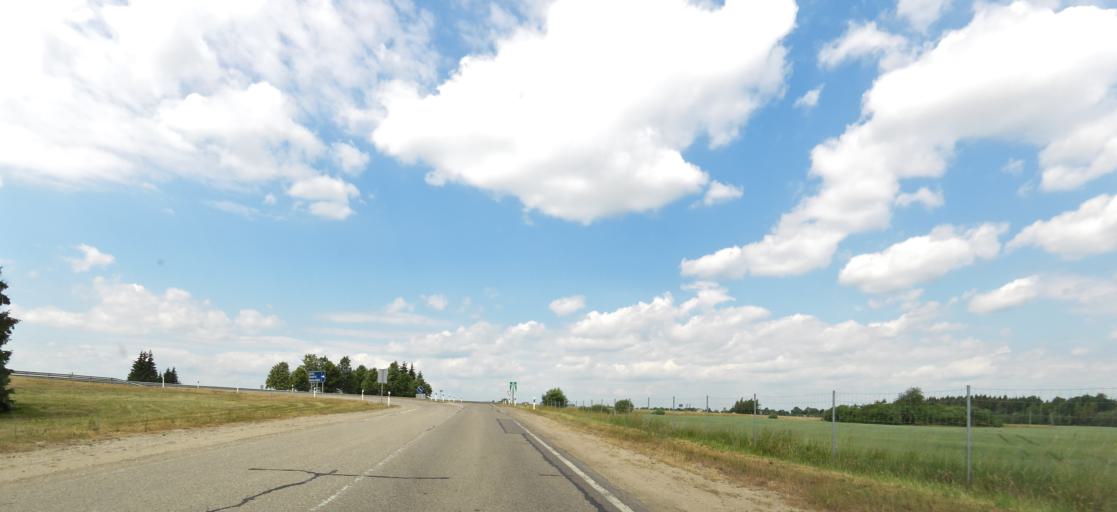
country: LT
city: Sirvintos
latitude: 55.0665
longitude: 24.8868
